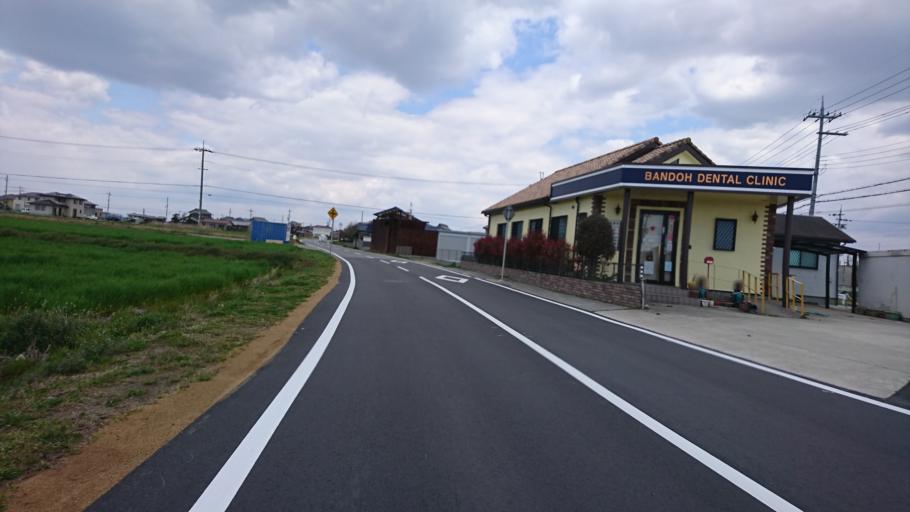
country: JP
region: Hyogo
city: Miki
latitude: 34.7436
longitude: 134.9340
